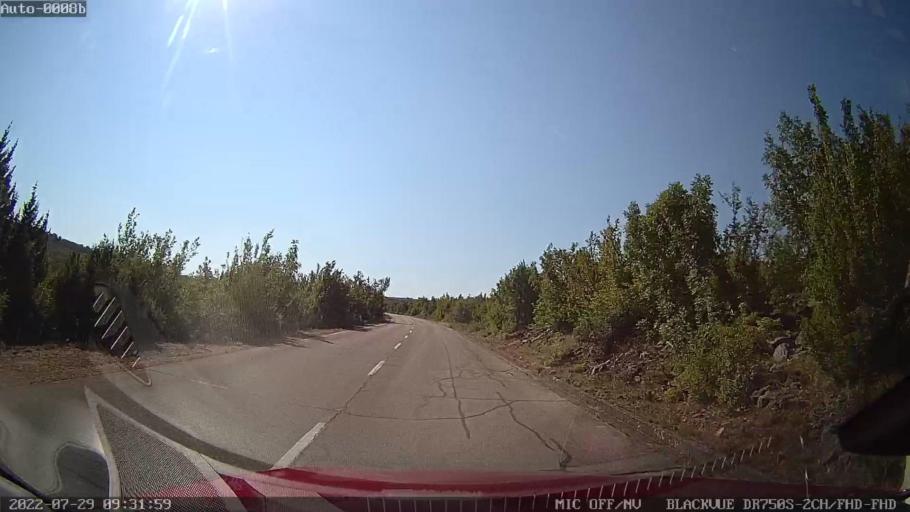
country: HR
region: Zadarska
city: Obrovac
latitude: 44.1849
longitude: 15.7055
